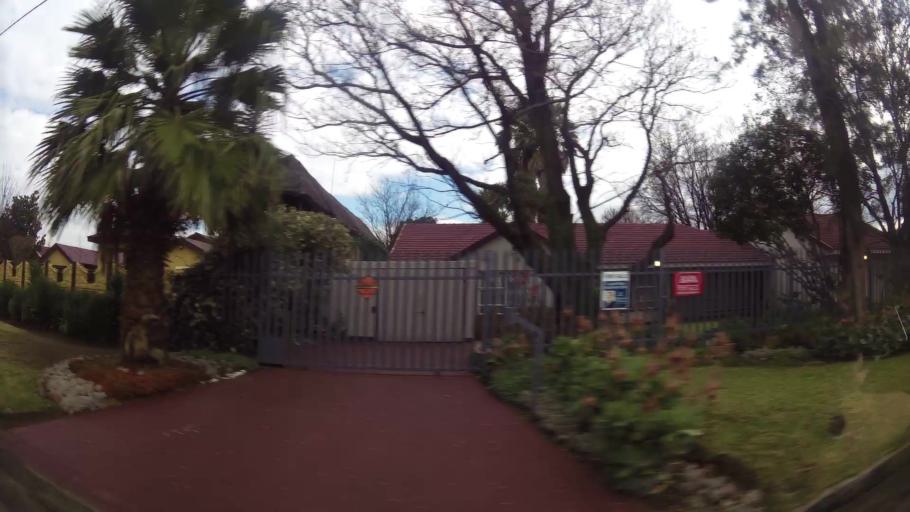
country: ZA
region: Gauteng
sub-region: Sedibeng District Municipality
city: Vereeniging
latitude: -26.6468
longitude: 27.9890
